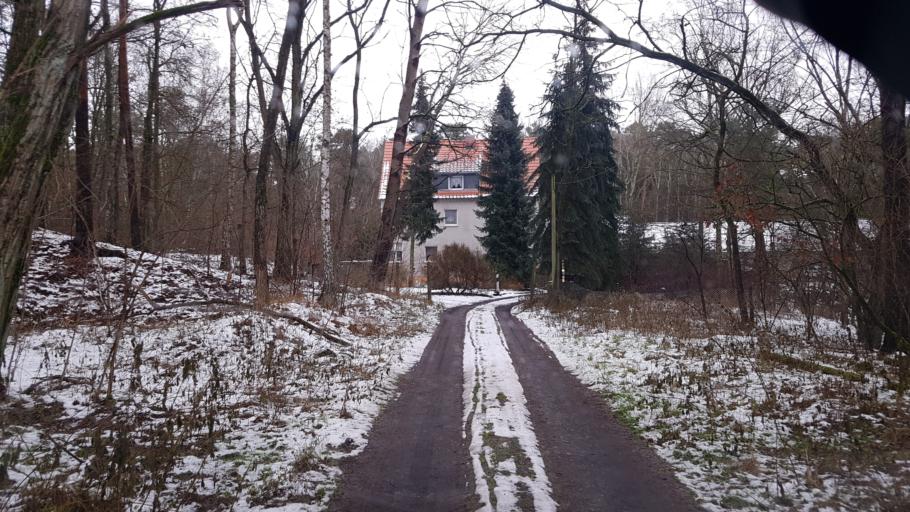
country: DE
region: Brandenburg
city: Schenkendobern
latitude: 51.9734
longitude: 14.5637
